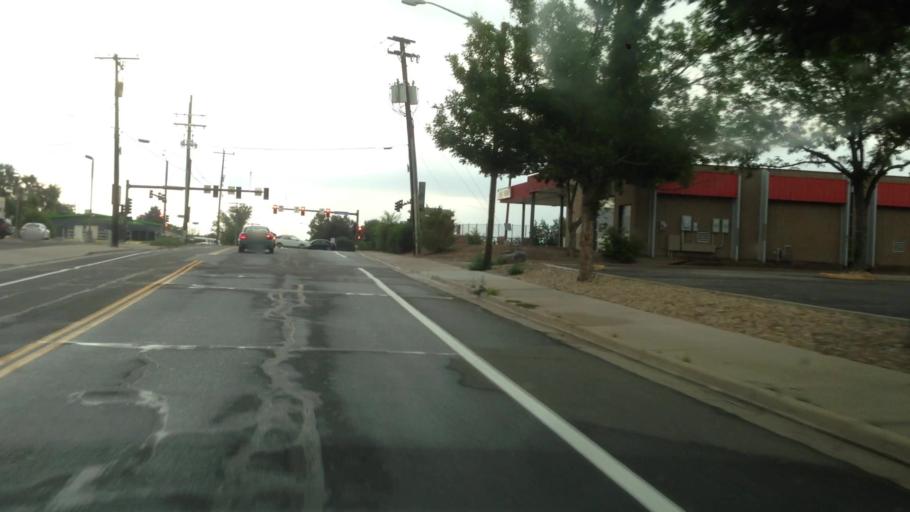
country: US
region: Colorado
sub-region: Jefferson County
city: Lakewood
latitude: 39.7099
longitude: -105.0627
